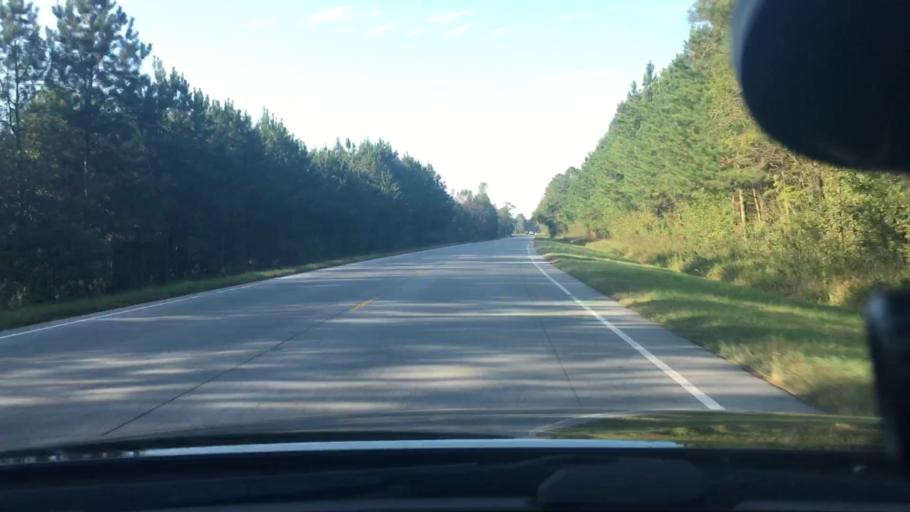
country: US
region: North Carolina
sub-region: Craven County
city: Vanceboro
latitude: 35.3214
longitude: -77.1456
